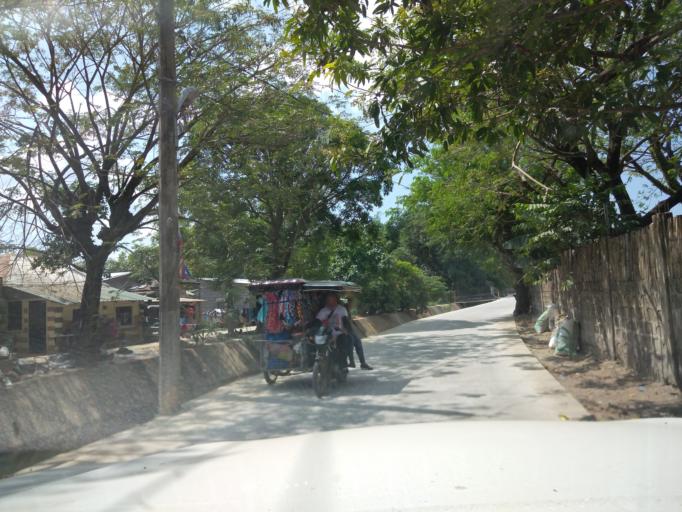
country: PH
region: Central Luzon
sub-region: Province of Pampanga
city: Bahay Pare
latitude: 15.0333
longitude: 120.8772
